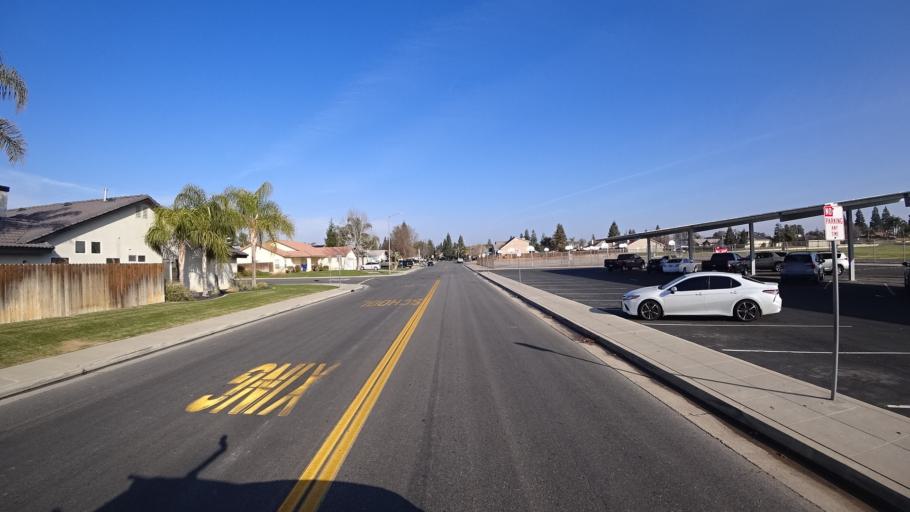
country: US
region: California
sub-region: Kern County
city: Oildale
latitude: 35.4015
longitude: -118.9387
